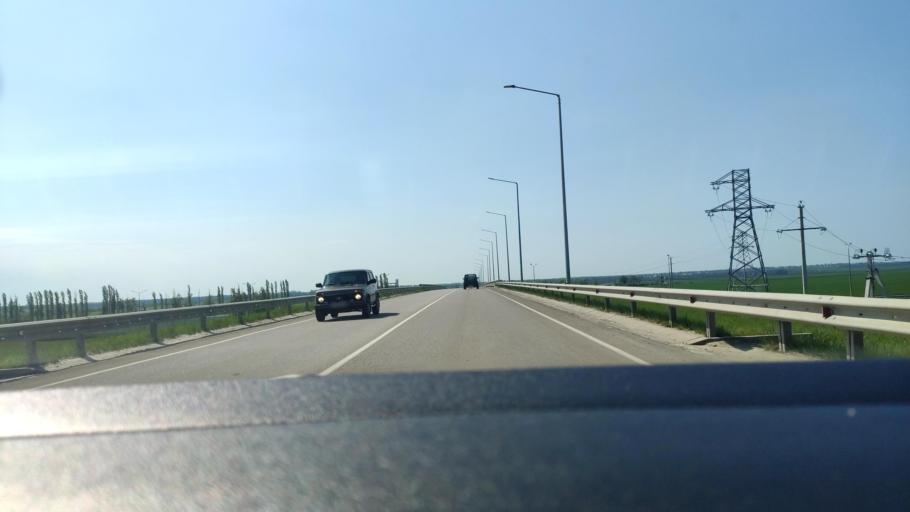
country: RU
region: Voronezj
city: Novaya Usman'
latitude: 51.5923
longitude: 39.3737
